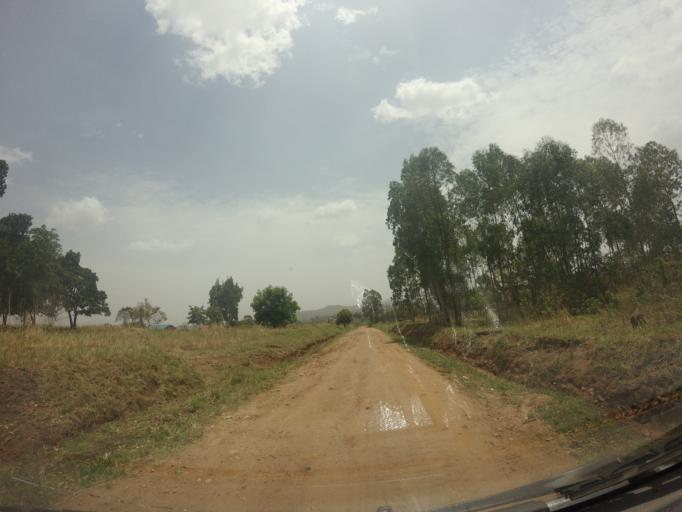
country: UG
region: Northern Region
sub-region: Arua District
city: Arua
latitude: 2.9370
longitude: 30.9156
